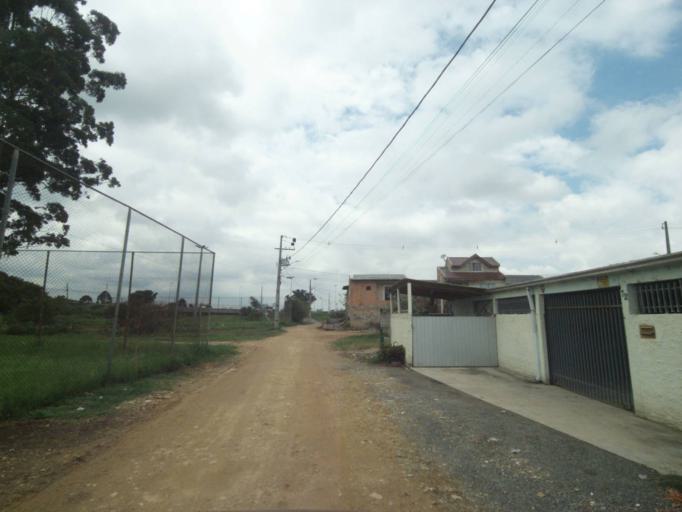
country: BR
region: Parana
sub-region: Pinhais
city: Pinhais
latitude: -25.4570
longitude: -49.1944
